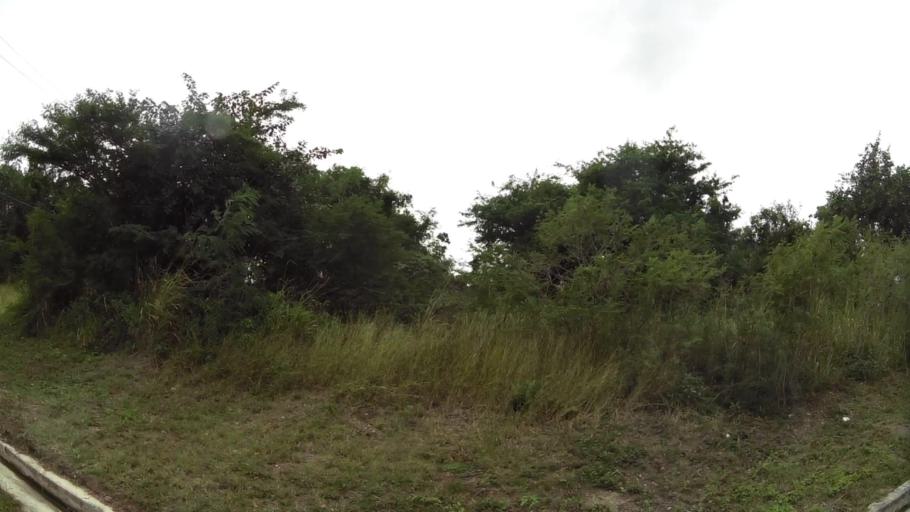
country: AG
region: Saint John
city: Potters Village
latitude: 17.0868
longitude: -61.8069
